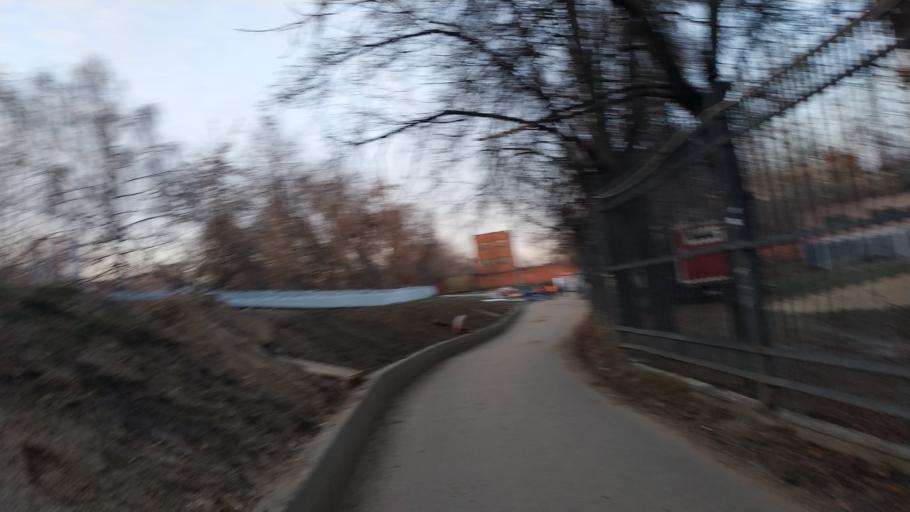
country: RU
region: Moscow
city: Pokrovskoye-Streshnevo
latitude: 55.8282
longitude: 37.4416
